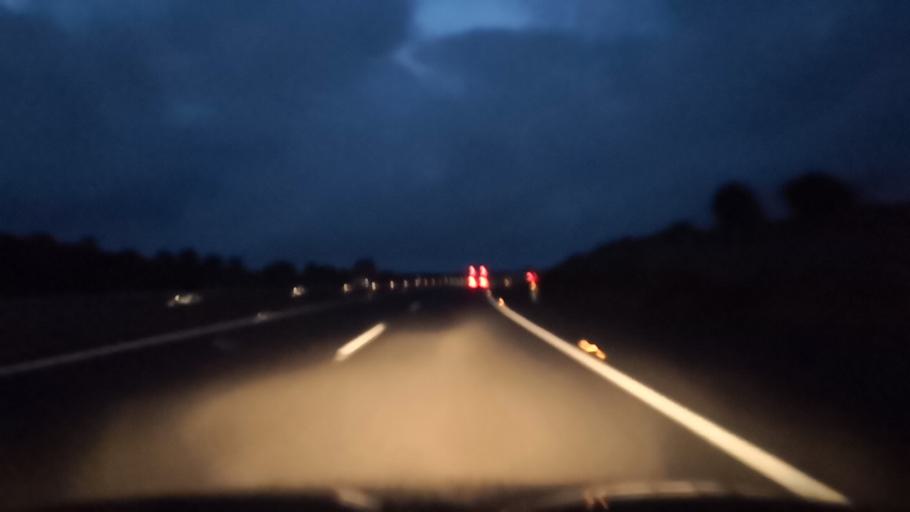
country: ES
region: Extremadura
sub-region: Provincia de Caceres
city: Caceres
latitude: 39.4812
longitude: -6.4356
